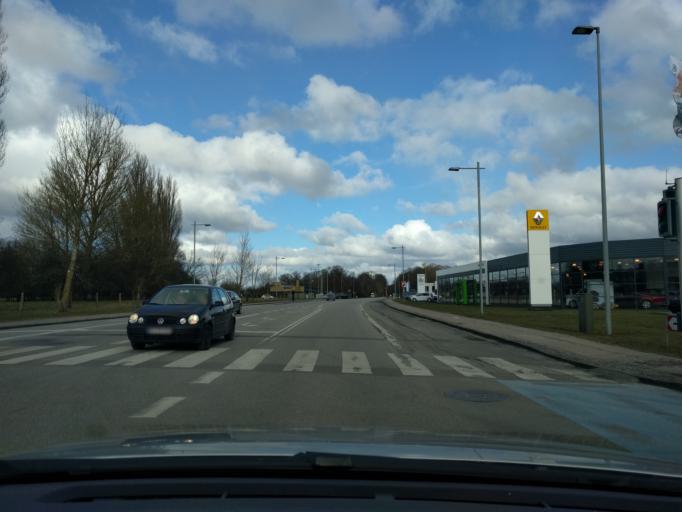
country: DK
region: Zealand
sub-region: Guldborgsund Kommune
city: Nykobing Falster
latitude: 54.7830
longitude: 11.8673
